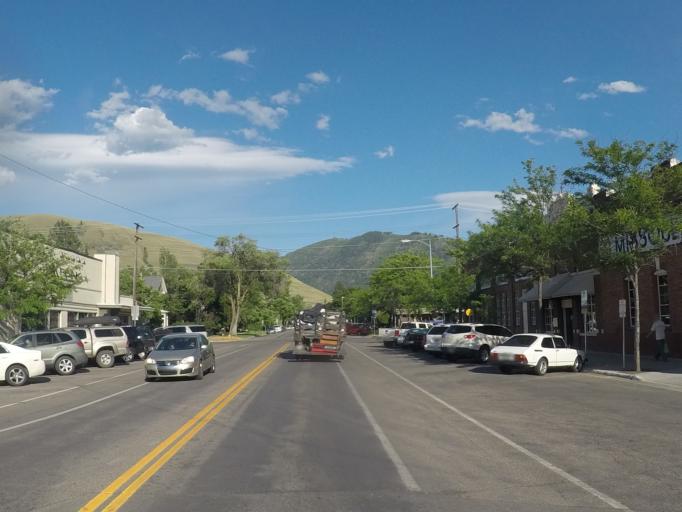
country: US
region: Montana
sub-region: Missoula County
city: Missoula
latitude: 46.8739
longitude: -113.9922
